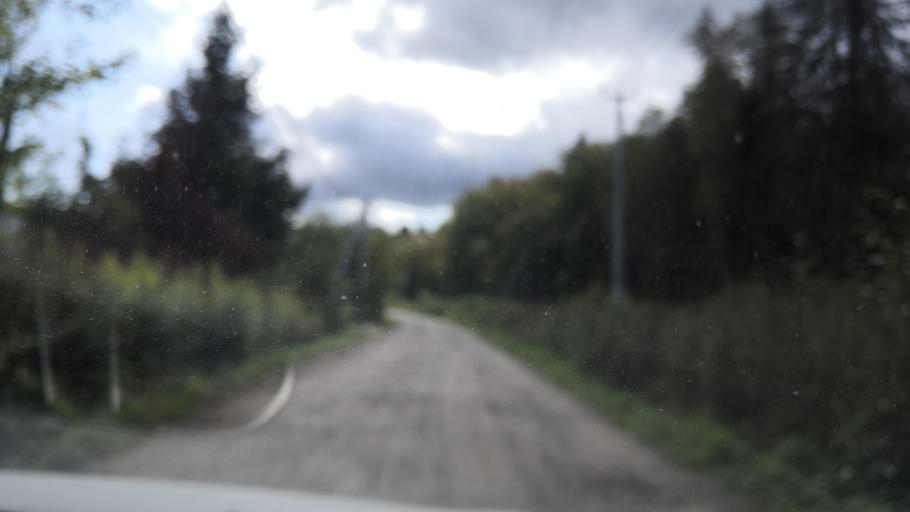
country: RU
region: Moskovskaya
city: Povarovo
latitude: 56.0583
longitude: 37.0204
